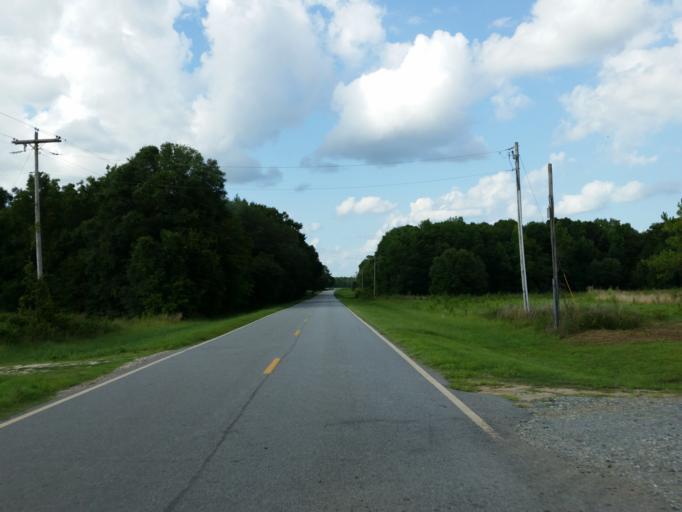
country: US
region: Georgia
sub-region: Lee County
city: Leesburg
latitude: 31.7429
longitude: -84.0439
